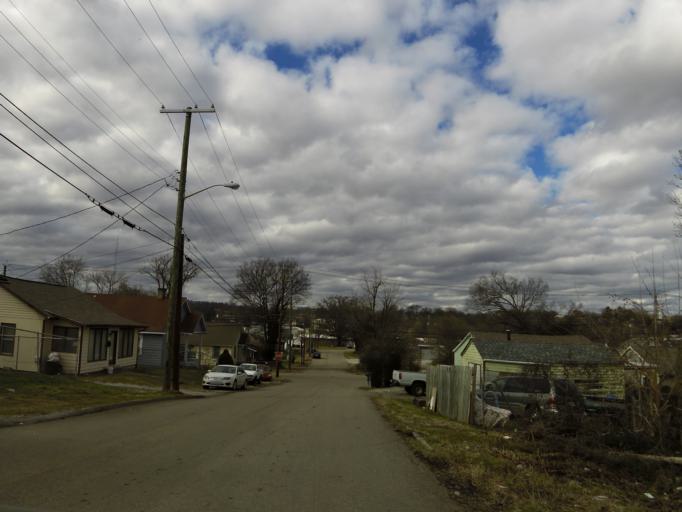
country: US
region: Tennessee
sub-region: Knox County
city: Knoxville
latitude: 35.9890
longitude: -83.9084
